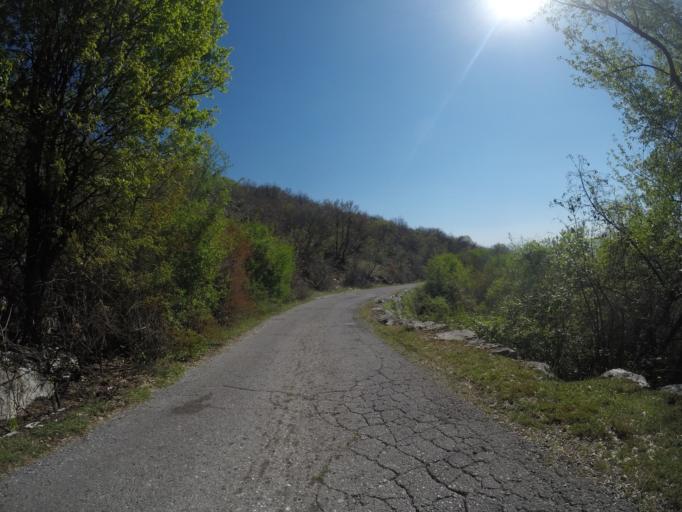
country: ME
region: Danilovgrad
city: Danilovgrad
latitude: 42.5172
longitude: 19.0598
